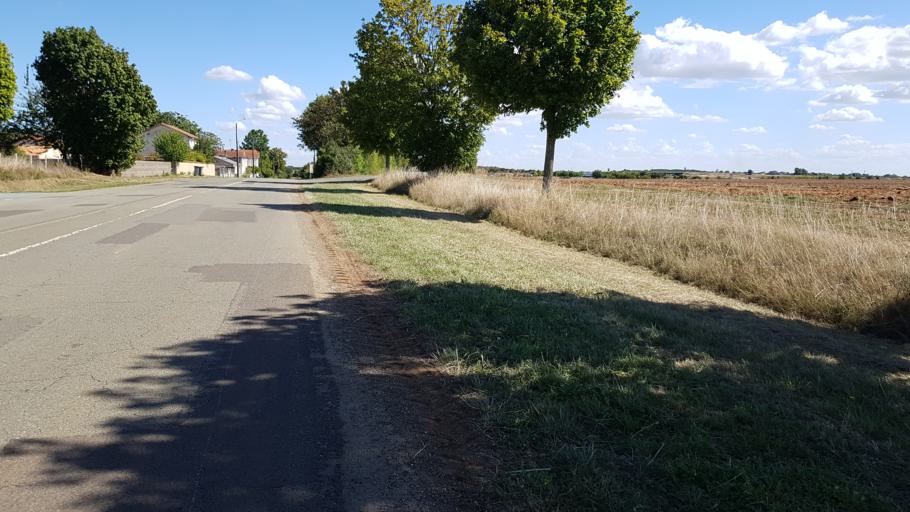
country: FR
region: Poitou-Charentes
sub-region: Departement des Deux-Sevres
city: Vouille
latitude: 46.3141
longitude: -0.3792
